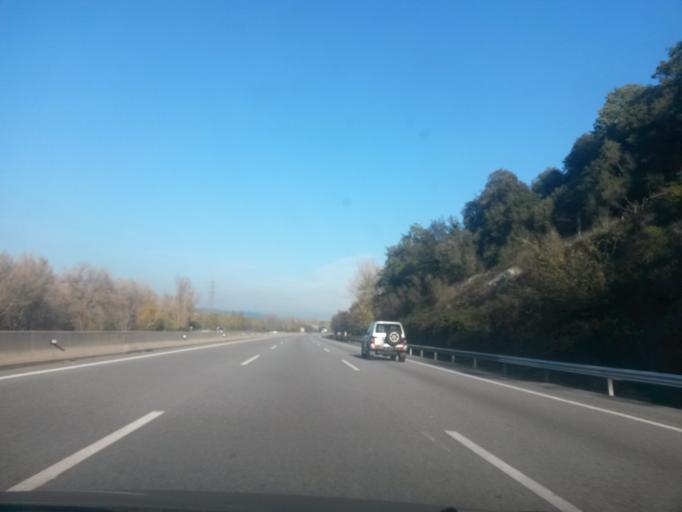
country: ES
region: Catalonia
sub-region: Provincia de Girona
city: Breda
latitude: 41.7088
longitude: 2.5328
